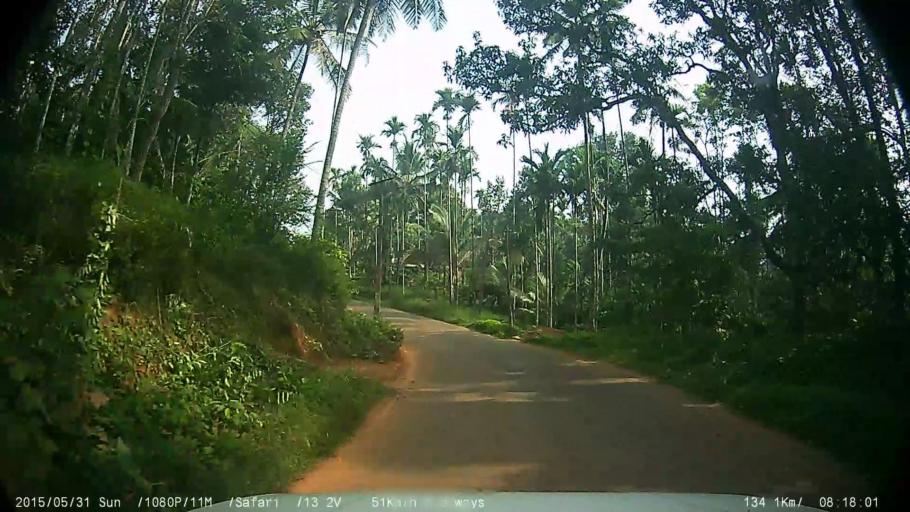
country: IN
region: Kerala
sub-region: Wayanad
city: Kalpetta
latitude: 11.6633
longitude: 75.9882
